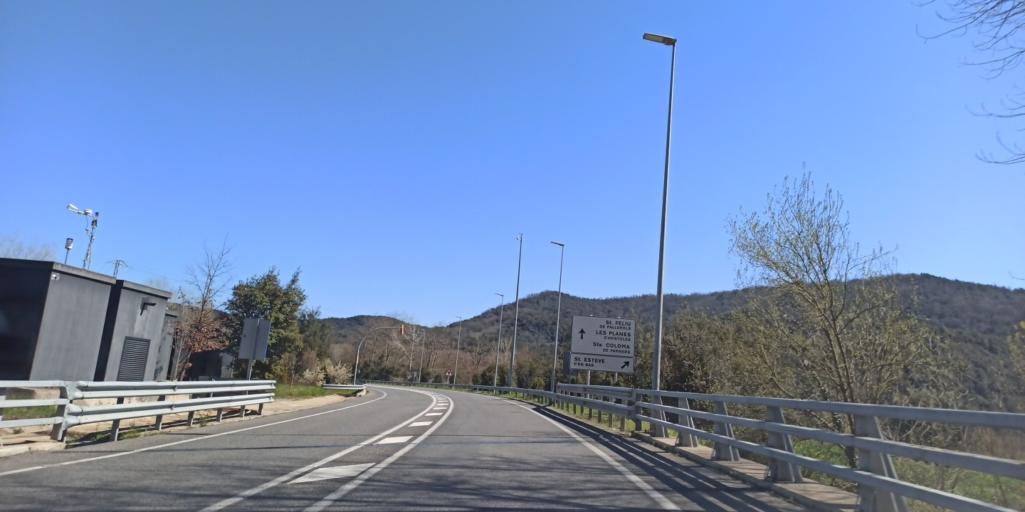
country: ES
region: Catalonia
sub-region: Provincia de Girona
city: Bas
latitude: 42.1236
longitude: 2.4605
